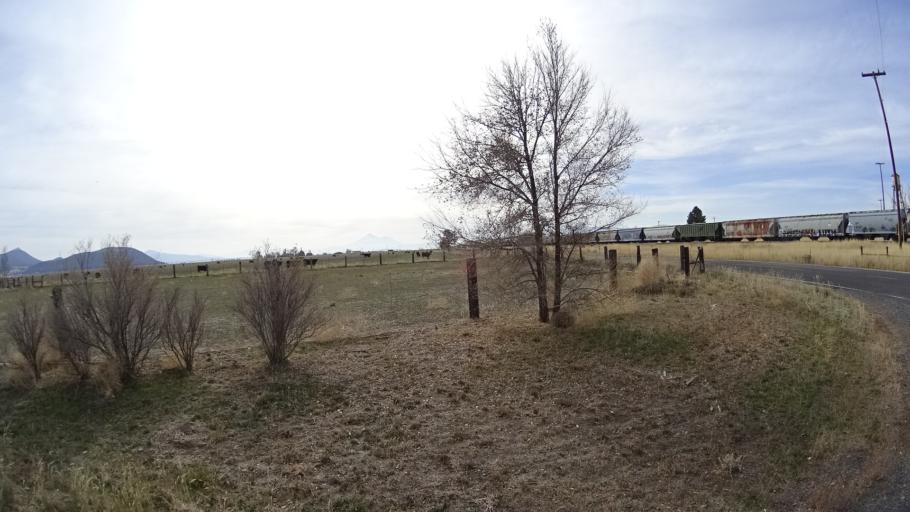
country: US
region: Oregon
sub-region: Klamath County
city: Klamath Falls
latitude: 41.9598
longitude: -121.9187
